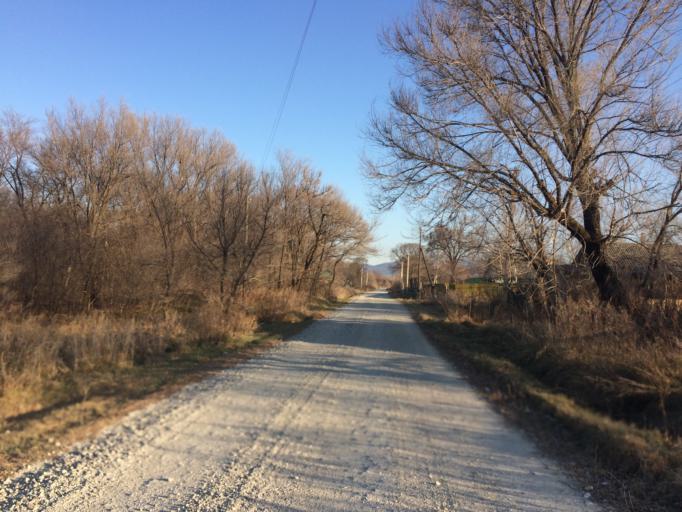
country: RU
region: Primorskiy
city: Ivanovka
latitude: 43.9571
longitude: 132.4789
